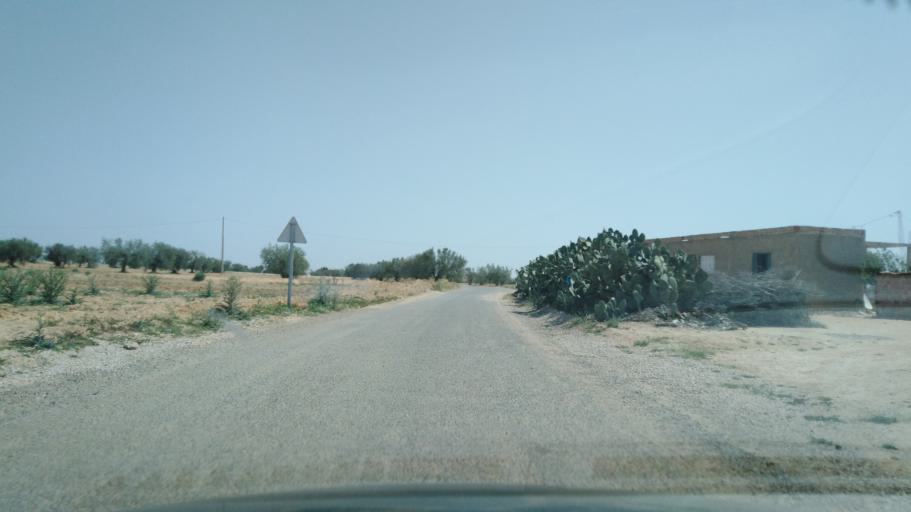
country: TN
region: Safaqis
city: Sfax
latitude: 34.6860
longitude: 10.4417
